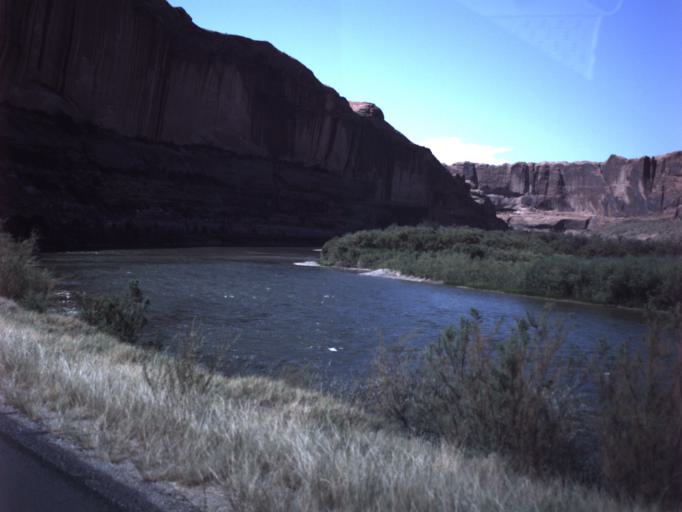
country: US
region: Utah
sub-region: Grand County
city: Moab
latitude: 38.6079
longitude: -109.5393
